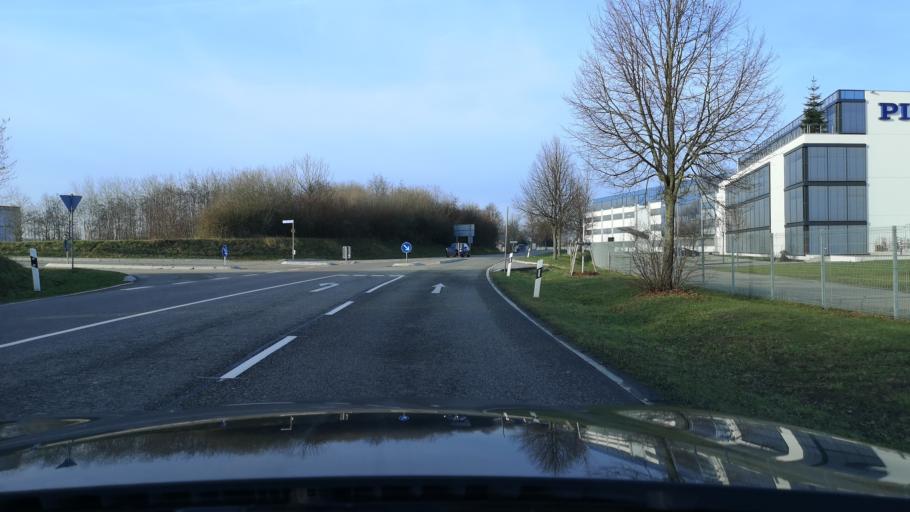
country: DE
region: Baden-Wuerttemberg
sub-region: Karlsruhe Region
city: Ettlingen
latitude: 48.9443
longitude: 8.4910
